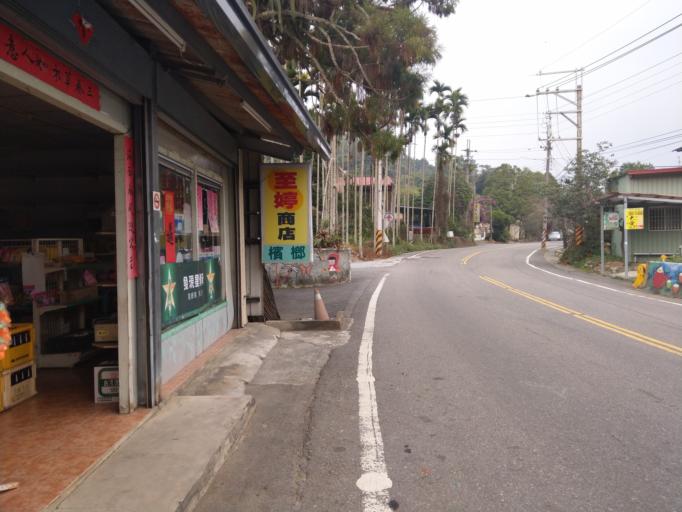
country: TW
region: Taiwan
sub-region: Nantou
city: Puli
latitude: 23.9041
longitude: 120.9173
